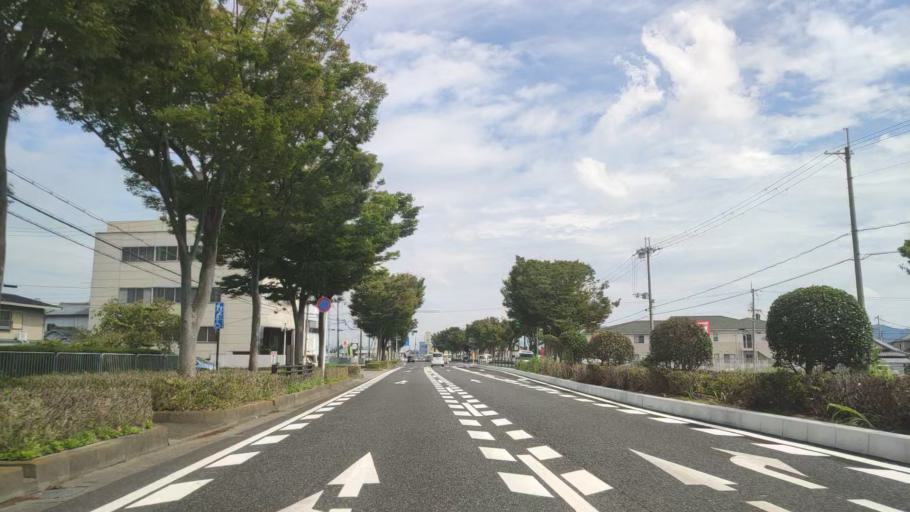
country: JP
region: Wakayama
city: Iwade
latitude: 34.2555
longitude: 135.2557
